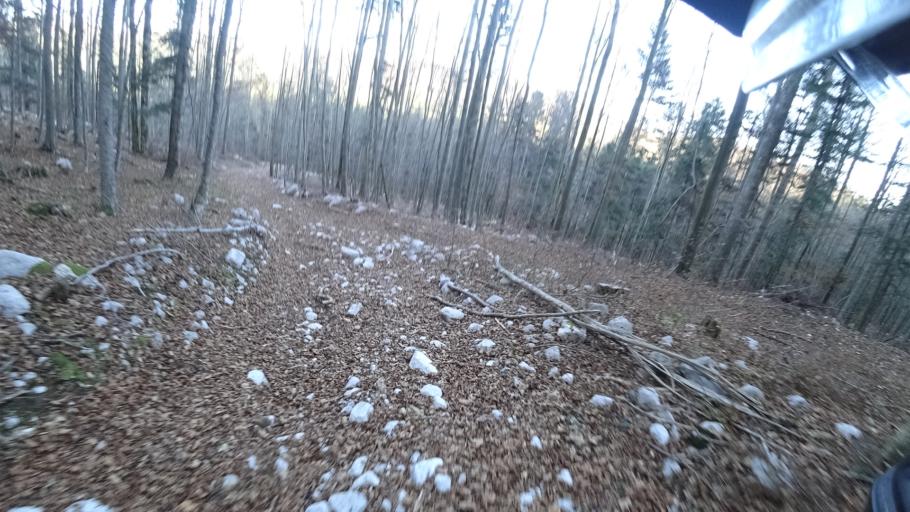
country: HR
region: Primorsko-Goranska
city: Klana
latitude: 45.4838
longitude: 14.4576
